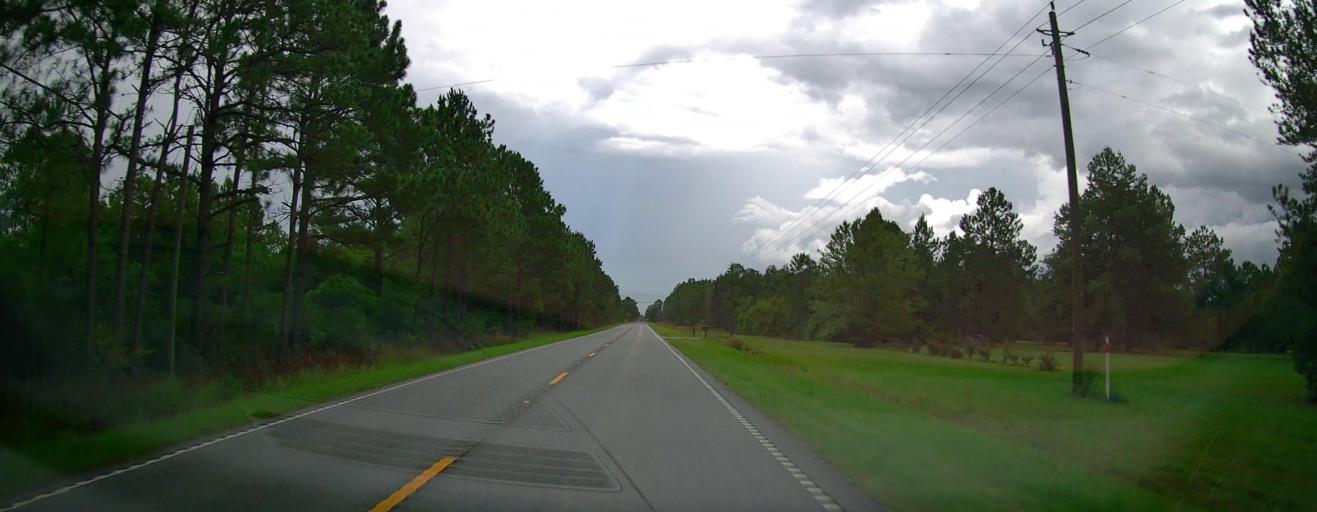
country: US
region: Georgia
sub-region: Pierce County
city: Blackshear
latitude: 31.3641
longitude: -82.0813
